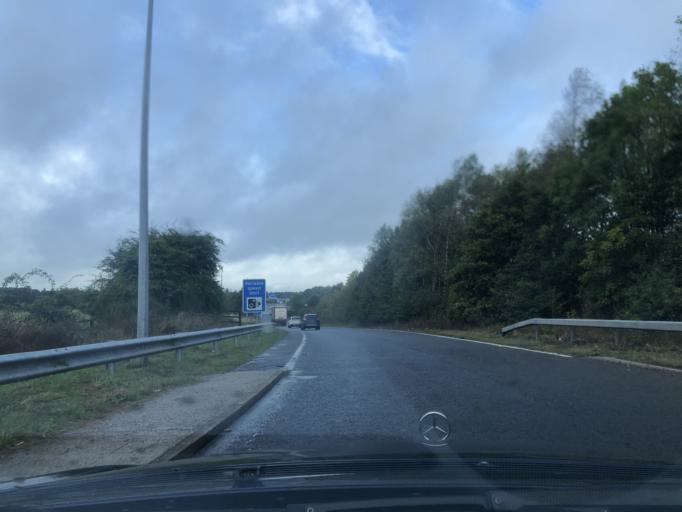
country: GB
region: England
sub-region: Warwickshire
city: Henley in Arden
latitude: 52.3341
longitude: -1.7728
